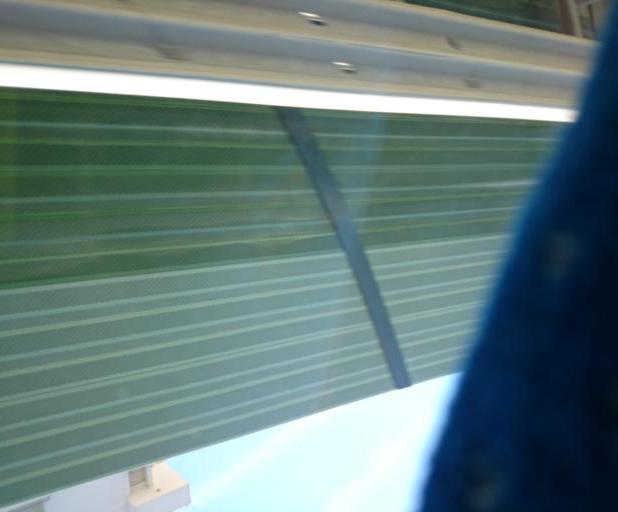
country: AL
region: Tirane
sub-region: Rrethi i Kavajes
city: Golem
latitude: 41.2683
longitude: 19.5209
